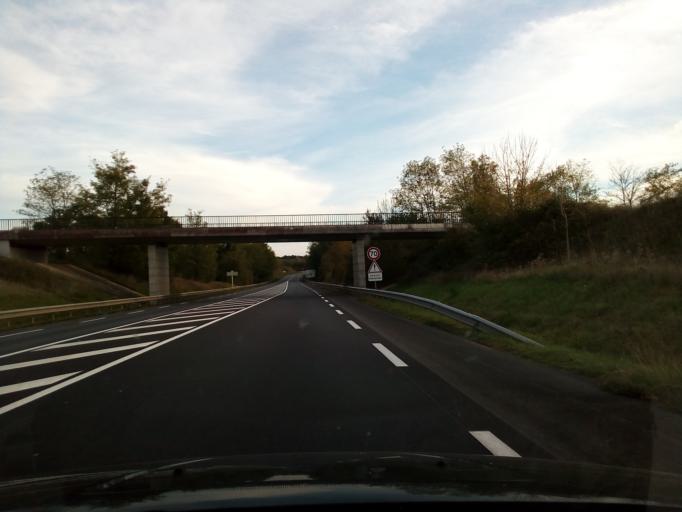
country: FR
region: Poitou-Charentes
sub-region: Departement de la Charente
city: Chasseneuil-sur-Bonnieure
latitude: 45.8356
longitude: 0.4656
